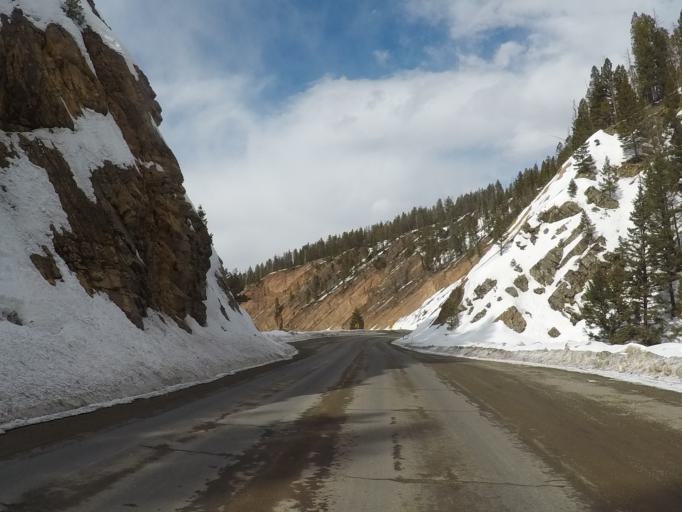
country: US
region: Montana
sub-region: Granite County
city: Philipsburg
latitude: 46.2201
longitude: -113.2880
